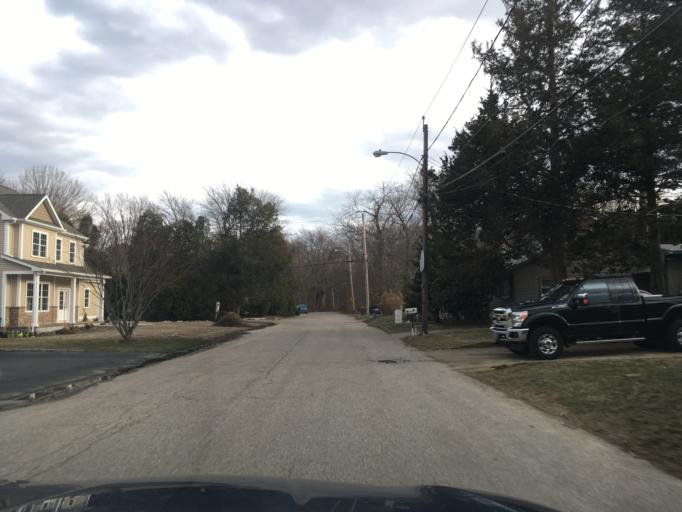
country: US
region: Rhode Island
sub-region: Kent County
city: East Greenwich
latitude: 41.6664
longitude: -71.4235
